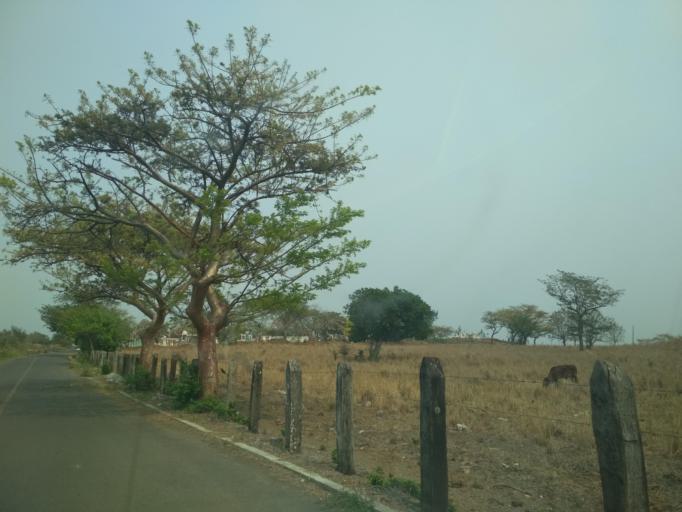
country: MX
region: Veracruz
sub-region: Veracruz
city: Delfino Victoria (Santa Fe)
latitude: 19.2185
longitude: -96.3112
